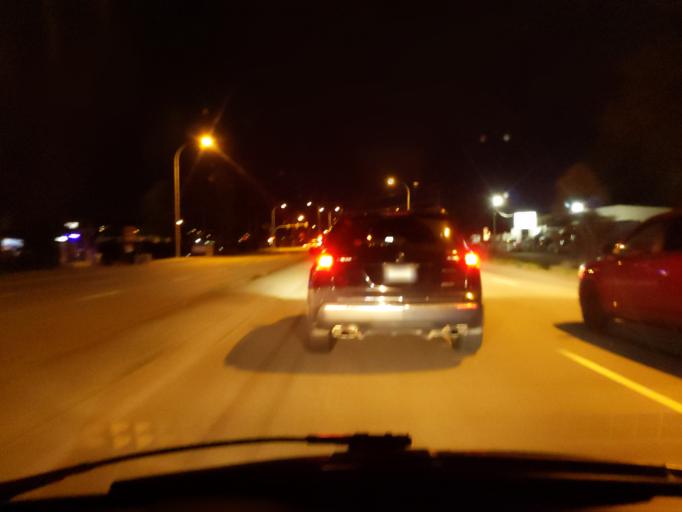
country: CA
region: British Columbia
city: New Westminster
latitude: 49.2006
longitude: -122.8813
